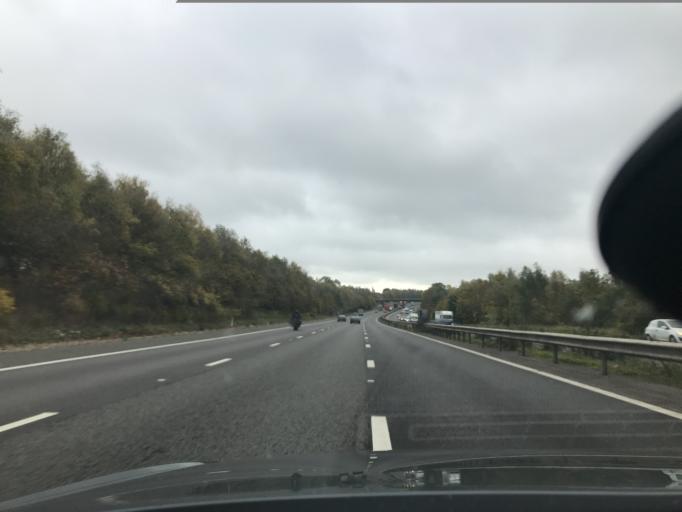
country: GB
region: England
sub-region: Warwickshire
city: Wroxall
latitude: 52.2924
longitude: -1.6784
